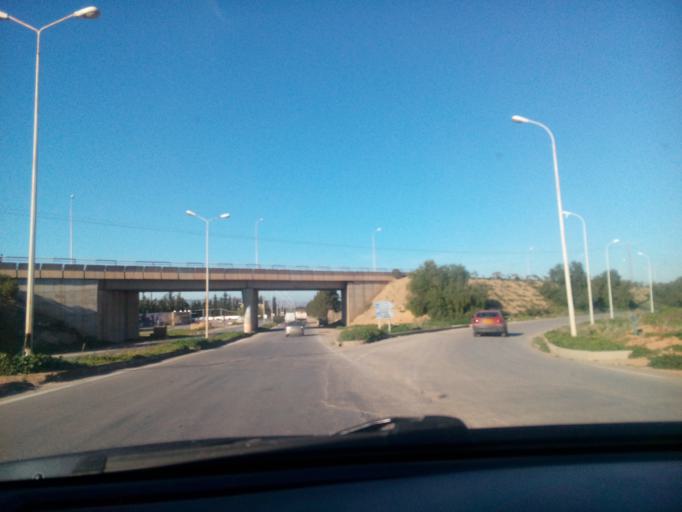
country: DZ
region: Relizane
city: Relizane
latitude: 35.7159
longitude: 0.5079
